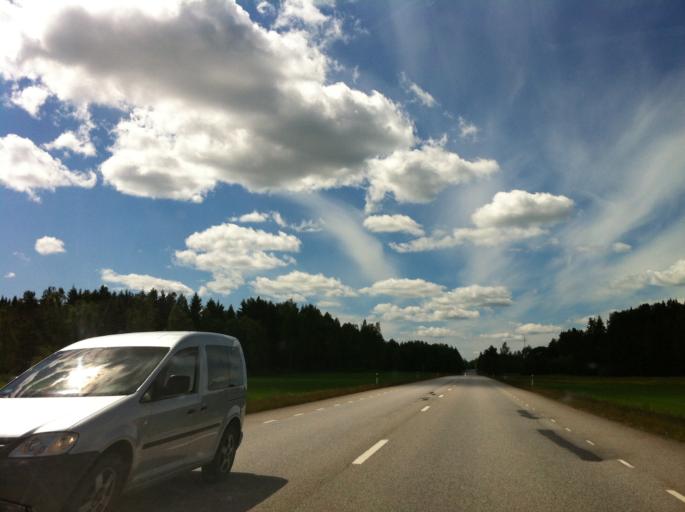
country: SE
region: Vaestra Goetaland
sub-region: Amals Kommun
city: Amal
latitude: 59.0054
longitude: 12.6862
